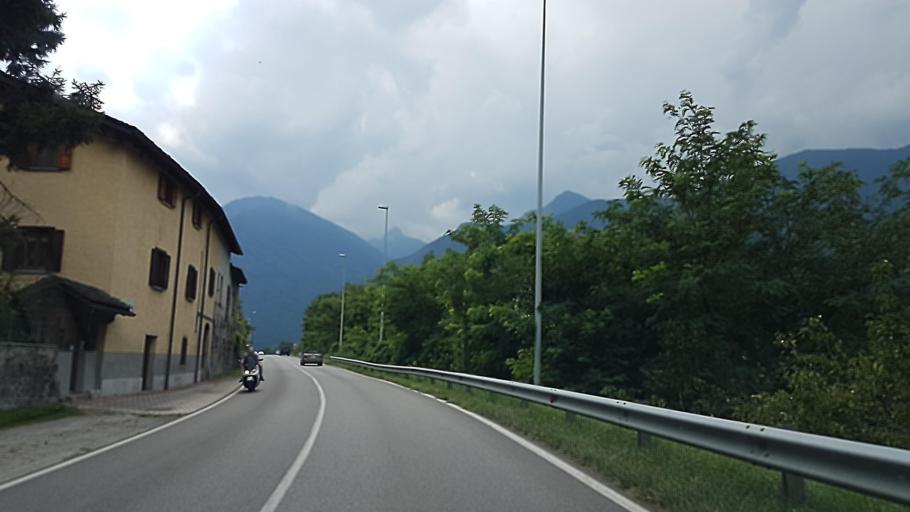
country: IT
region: Lombardy
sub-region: Provincia di Sondrio
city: Prata Camportaccio
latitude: 46.3080
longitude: 9.3925
